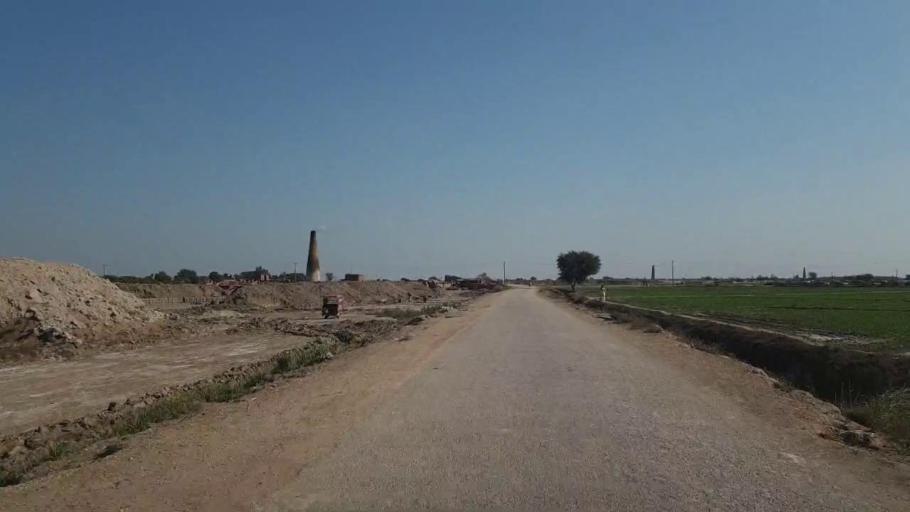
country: PK
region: Sindh
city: Tando Allahyar
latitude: 25.4143
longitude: 68.7001
